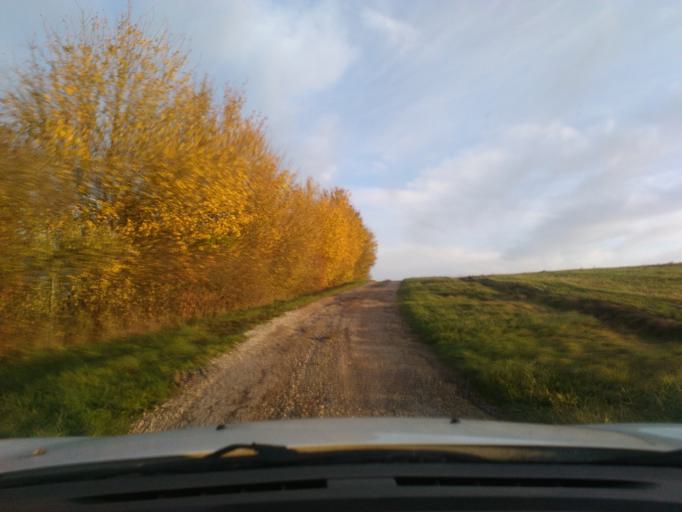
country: FR
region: Lorraine
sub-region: Departement des Vosges
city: Mirecourt
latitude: 48.2531
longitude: 6.1745
